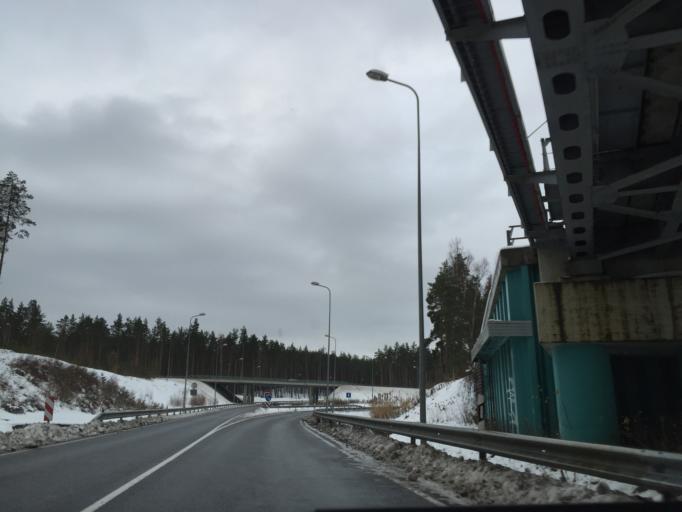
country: LV
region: Saulkrastu
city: Saulkrasti
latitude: 57.1965
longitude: 24.3640
